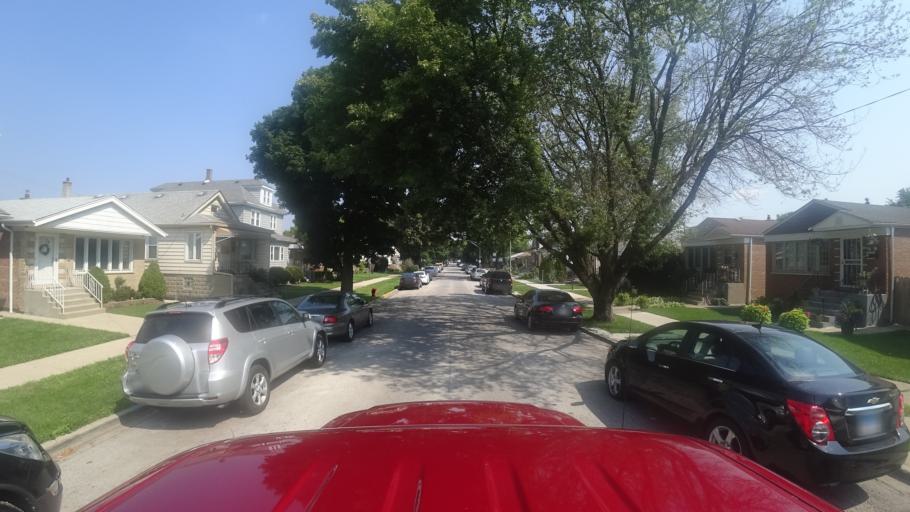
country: US
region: Illinois
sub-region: Cook County
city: Cicero
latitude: 41.7974
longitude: -87.7319
